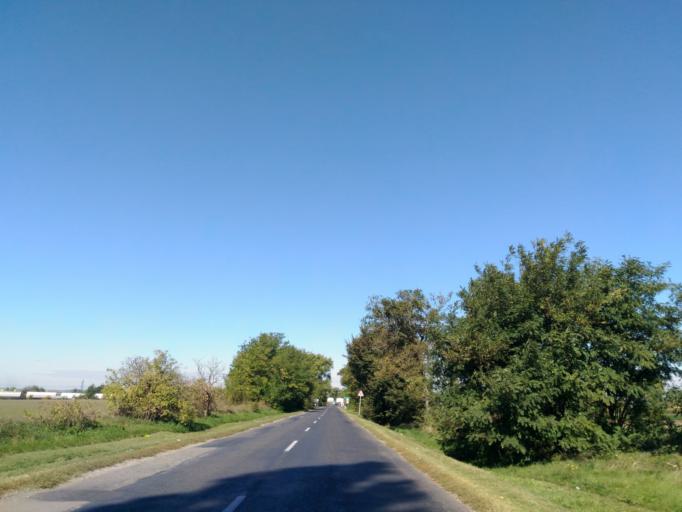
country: HU
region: Fejer
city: Ivancsa
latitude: 47.1735
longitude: 18.8134
